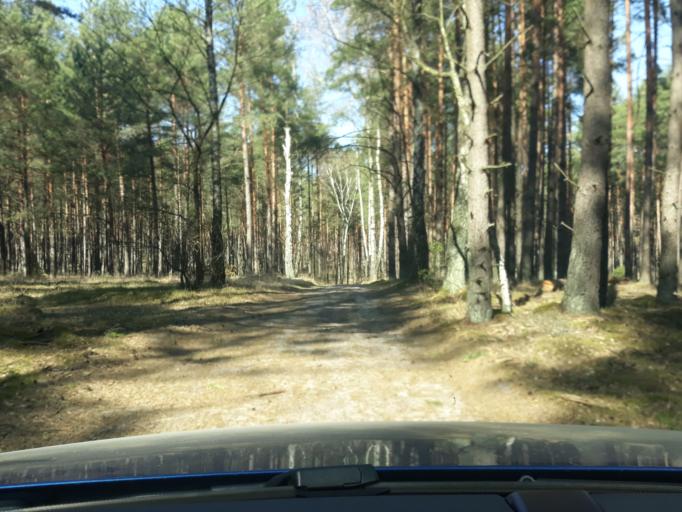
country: PL
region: Pomeranian Voivodeship
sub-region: Powiat bytowski
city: Lipnica
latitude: 53.8638
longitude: 17.4291
